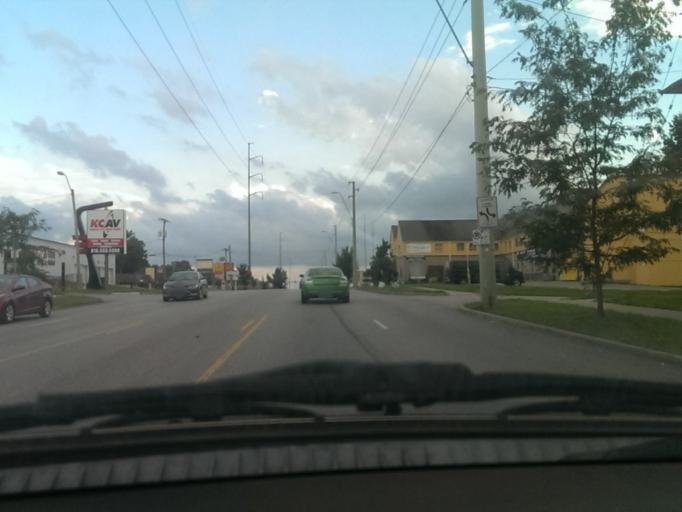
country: US
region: Kansas
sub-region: Johnson County
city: Leawood
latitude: 38.9909
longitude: -94.5758
